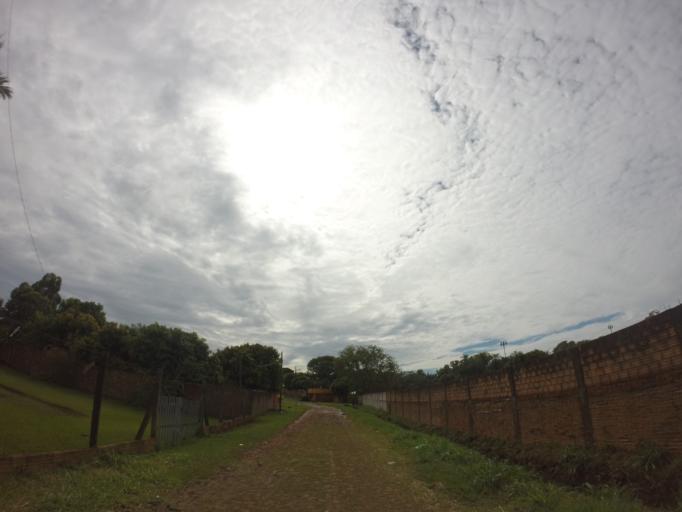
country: PY
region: Alto Parana
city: Ciudad del Este
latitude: -25.4083
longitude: -54.6397
